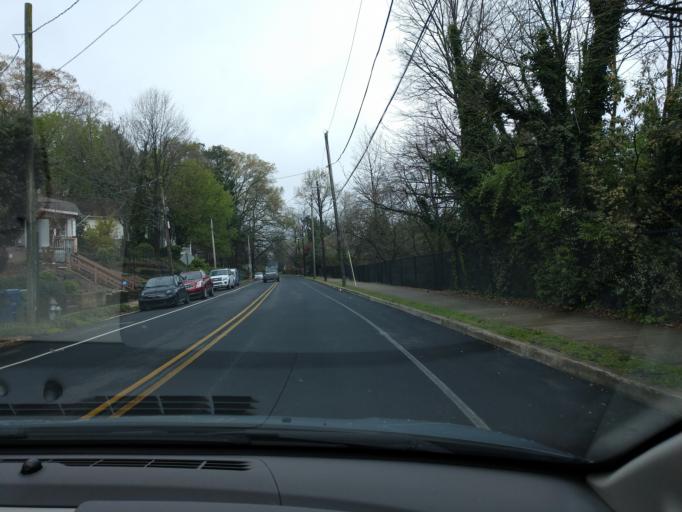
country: US
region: Georgia
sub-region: Fulton County
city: Atlanta
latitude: 33.7345
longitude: -84.3653
